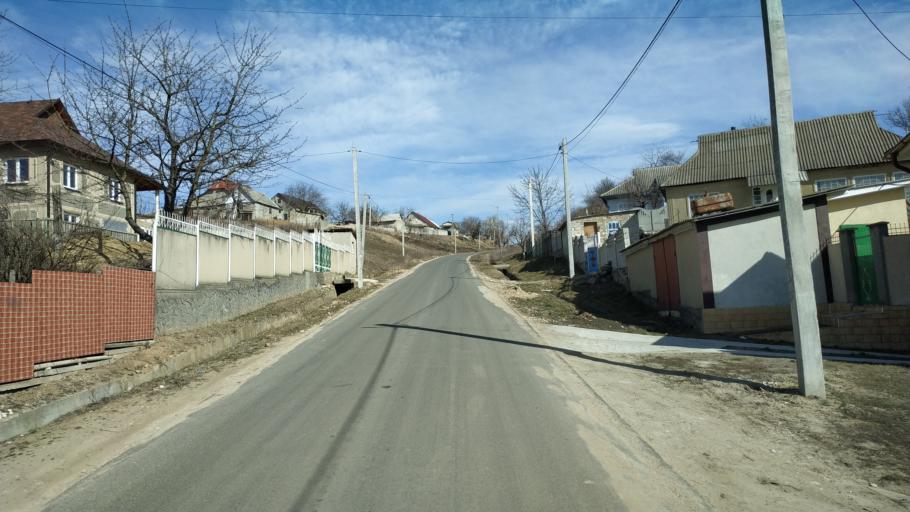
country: MD
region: Nisporeni
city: Nisporeni
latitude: 47.0993
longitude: 28.2937
